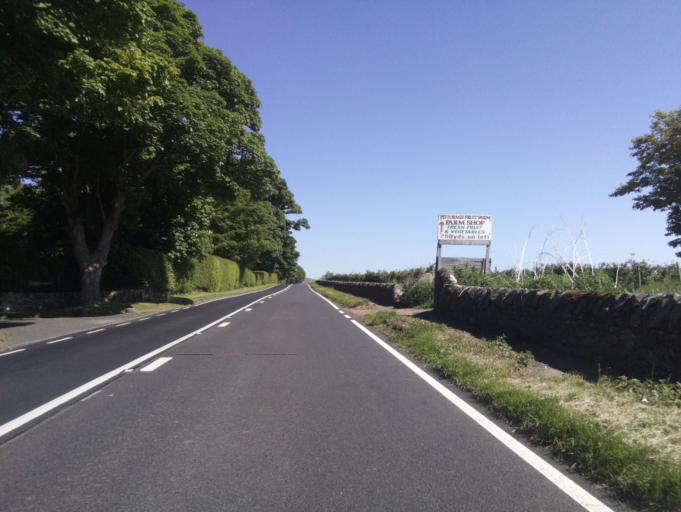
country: GB
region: Scotland
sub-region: Fife
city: Balmullo
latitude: 56.3546
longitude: -2.9413
